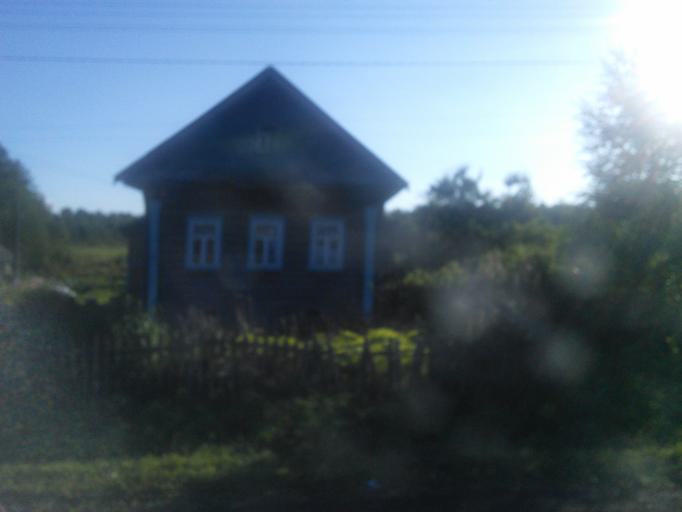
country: RU
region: Jaroslavl
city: Poshekhon'ye
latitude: 58.3744
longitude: 39.0034
